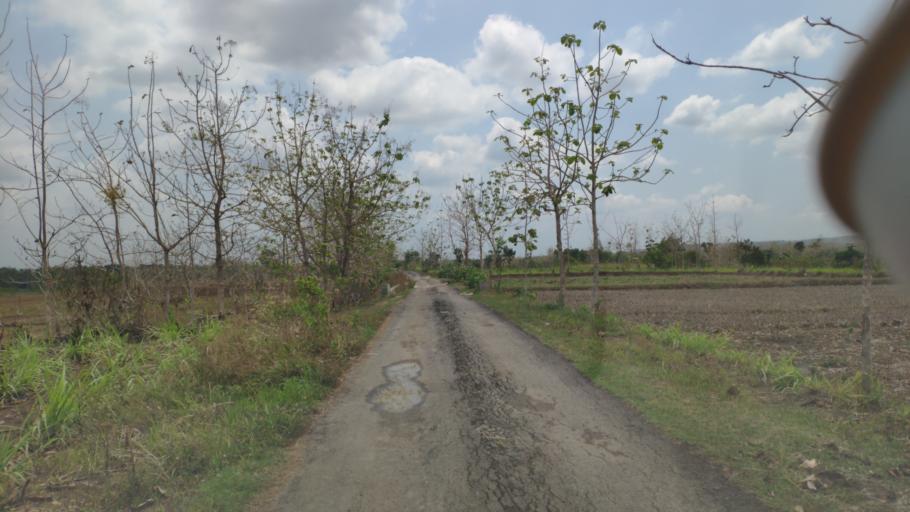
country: ID
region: Central Java
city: Klopoduwur
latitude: -7.0293
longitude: 111.4030
